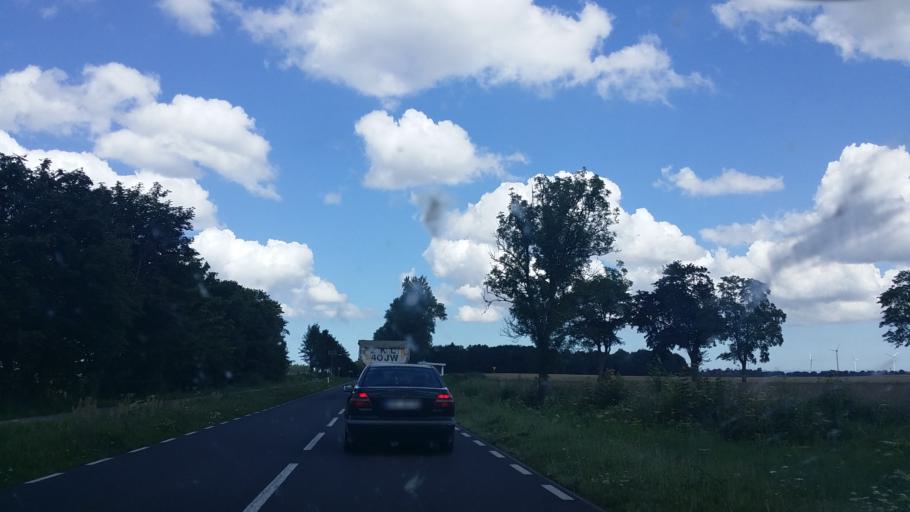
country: PL
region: West Pomeranian Voivodeship
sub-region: Powiat kolobrzeski
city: Goscino
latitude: 54.0172
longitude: 15.6603
